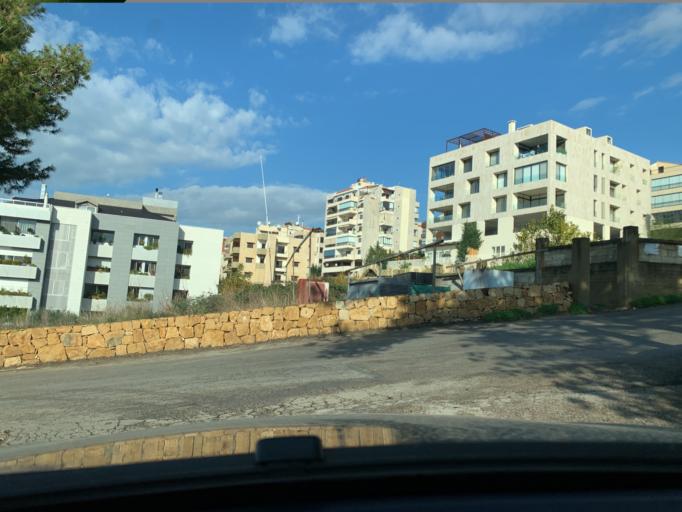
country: LB
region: Mont-Liban
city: Baabda
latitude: 33.8512
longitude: 35.5663
